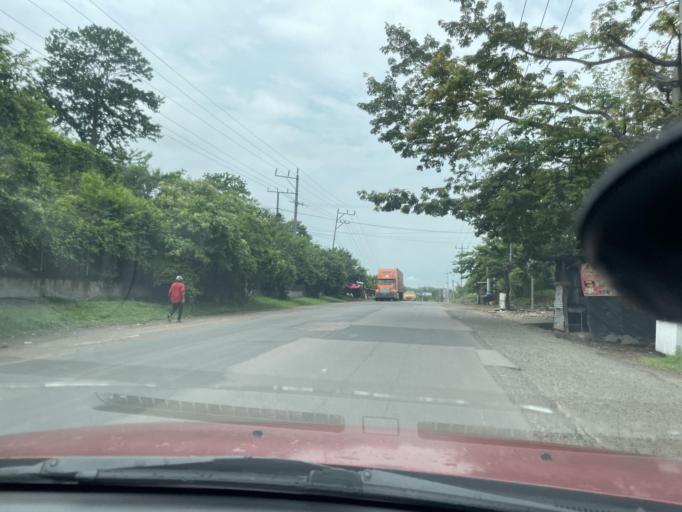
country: SV
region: La Union
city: Santa Rosa de Lima
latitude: 13.6210
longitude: -87.8642
